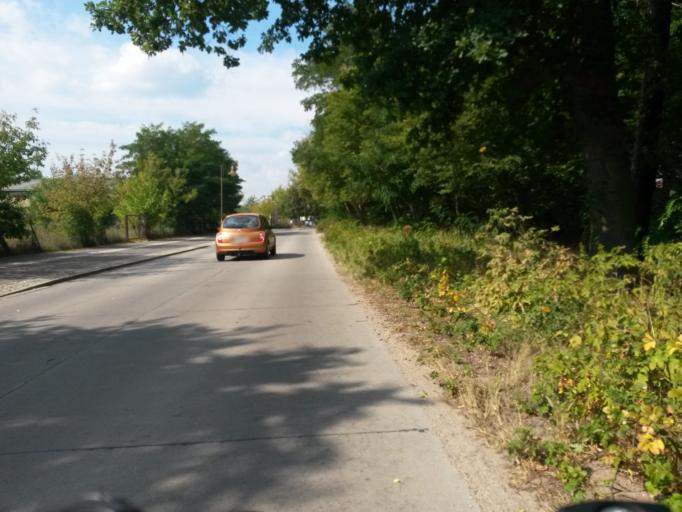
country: DE
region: Brandenburg
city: Templin
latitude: 53.1071
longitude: 13.5206
